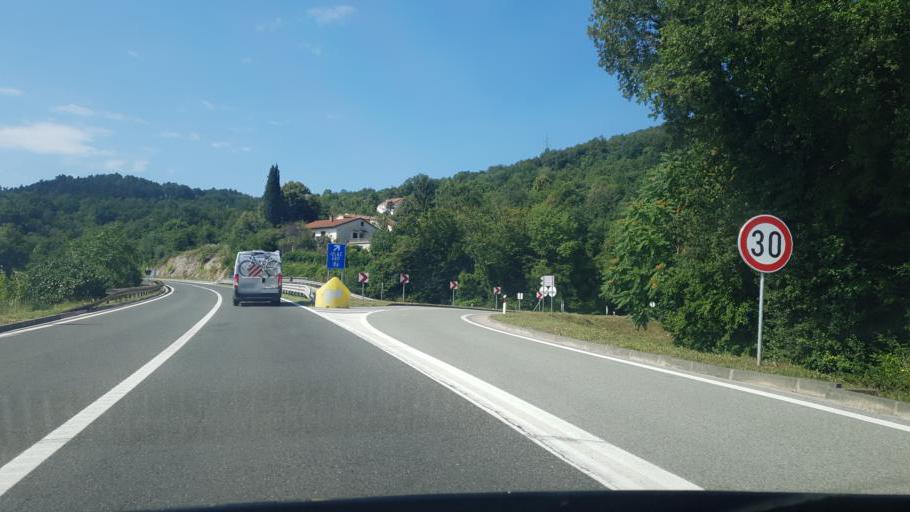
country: HR
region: Primorsko-Goranska
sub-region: Grad Opatija
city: Opatija
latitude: 45.3392
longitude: 14.2878
